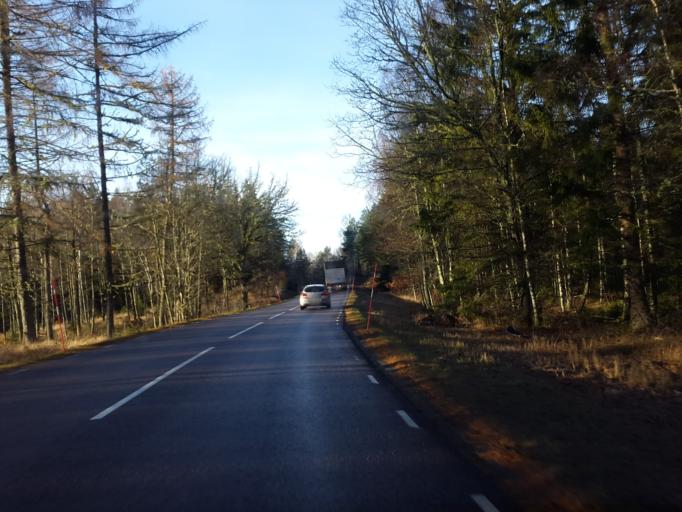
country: SE
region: Vaestra Goetaland
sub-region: Vargarda Kommun
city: Vargarda
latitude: 57.9901
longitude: 12.8246
